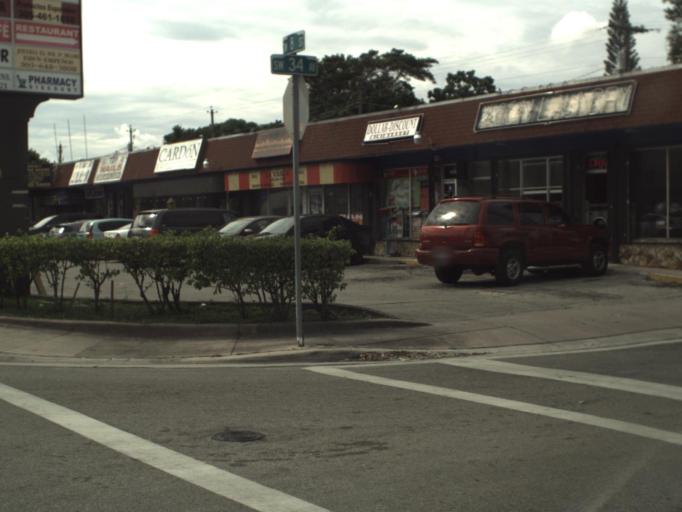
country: US
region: Florida
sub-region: Miami-Dade County
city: West Miami
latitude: 25.7649
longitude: -80.2511
